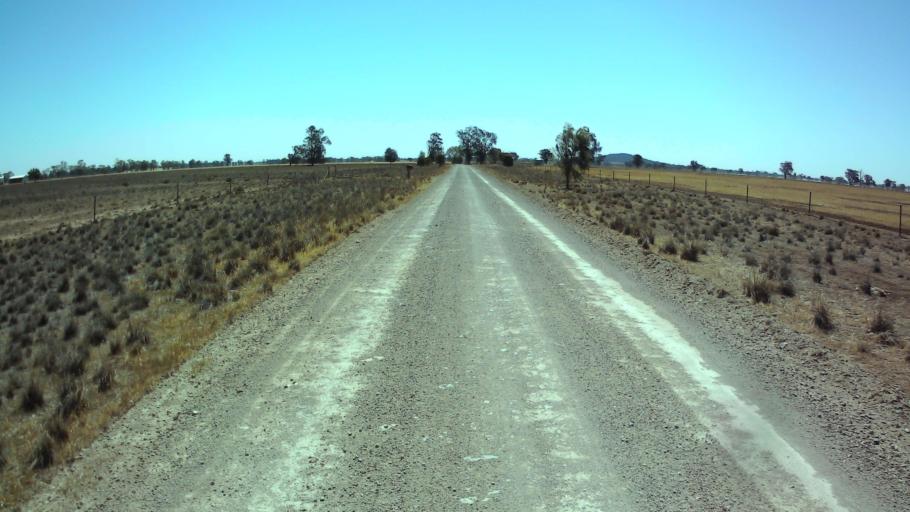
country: AU
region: New South Wales
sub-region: Forbes
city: Forbes
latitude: -33.7462
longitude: 147.7178
